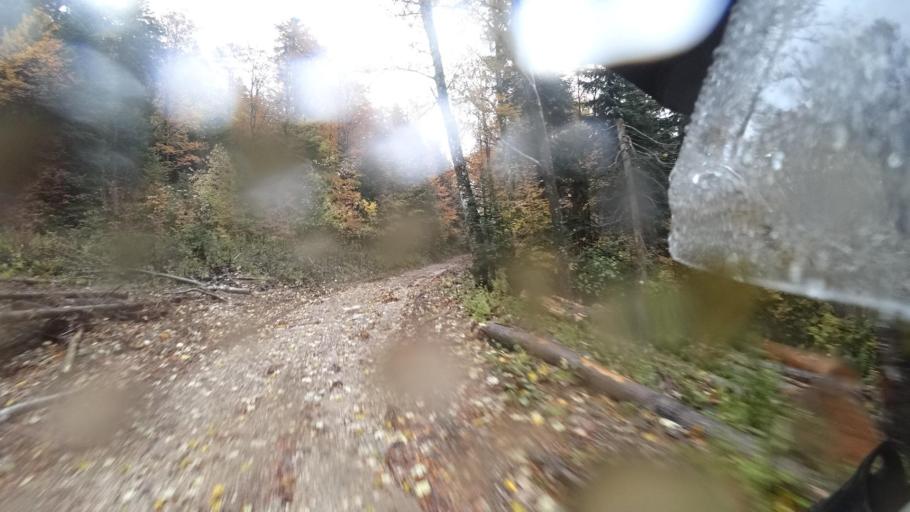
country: HR
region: Primorsko-Goranska
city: Vrbovsko
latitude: 45.3013
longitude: 15.0144
